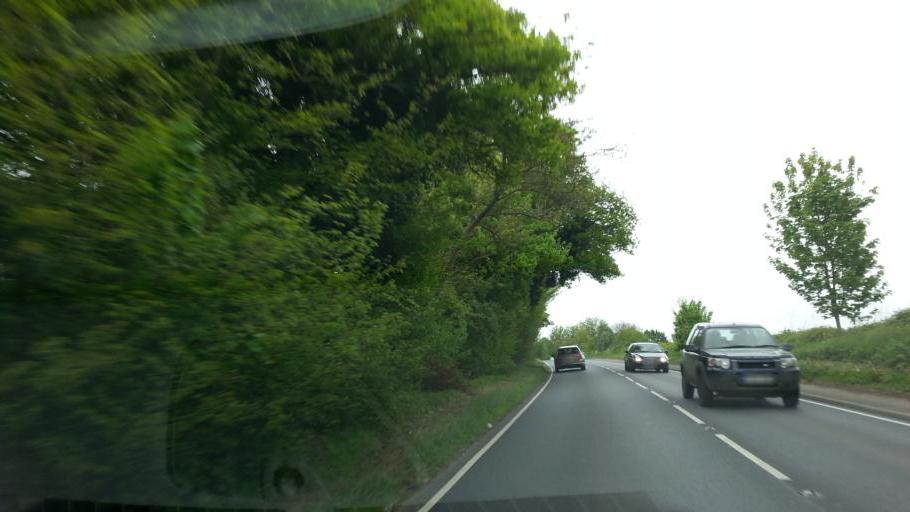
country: GB
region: England
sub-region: Suffolk
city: Bury St Edmunds
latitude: 52.2146
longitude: 0.7454
